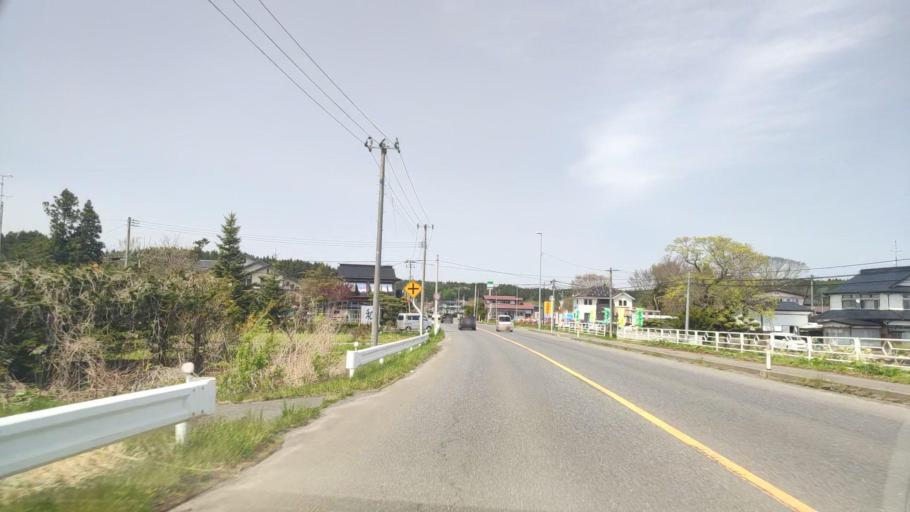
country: JP
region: Aomori
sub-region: Misawa Shi
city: Inuotose
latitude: 40.5577
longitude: 141.3876
